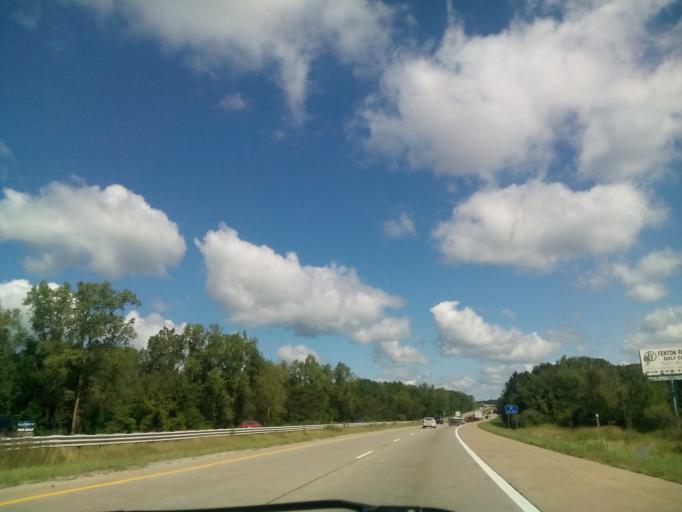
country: US
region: Michigan
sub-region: Genesee County
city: Lake Fenton
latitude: 42.8483
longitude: -83.7393
